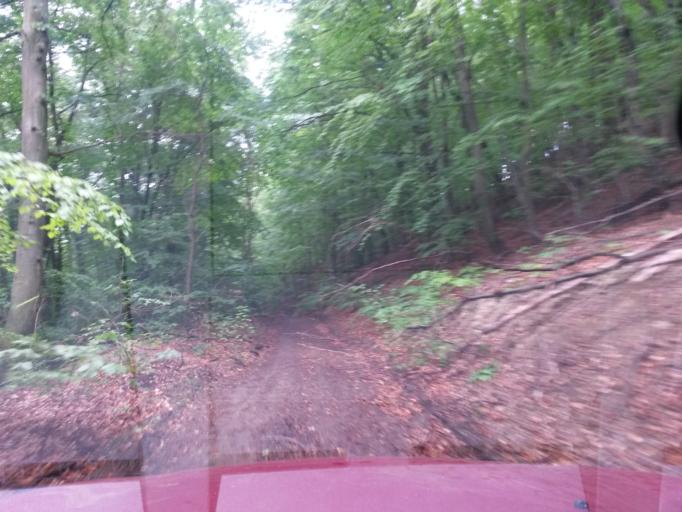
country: SK
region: Kosicky
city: Kosice
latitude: 48.7226
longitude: 21.1574
